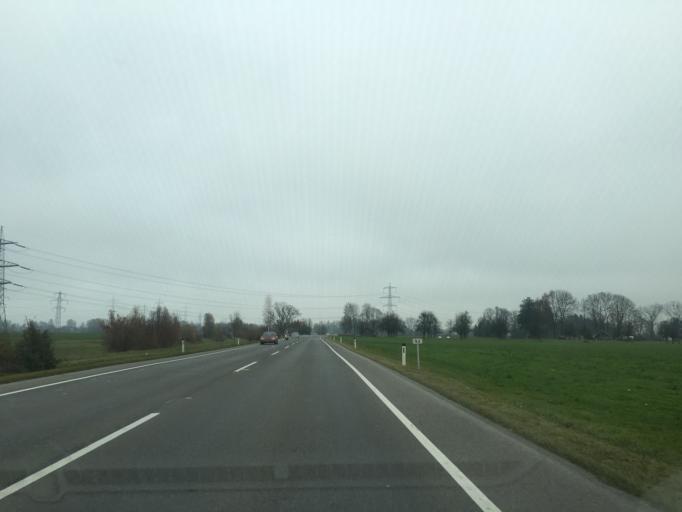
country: AT
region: Vorarlberg
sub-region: Politischer Bezirk Dornbirn
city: Hohenems
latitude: 47.3830
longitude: 9.6815
